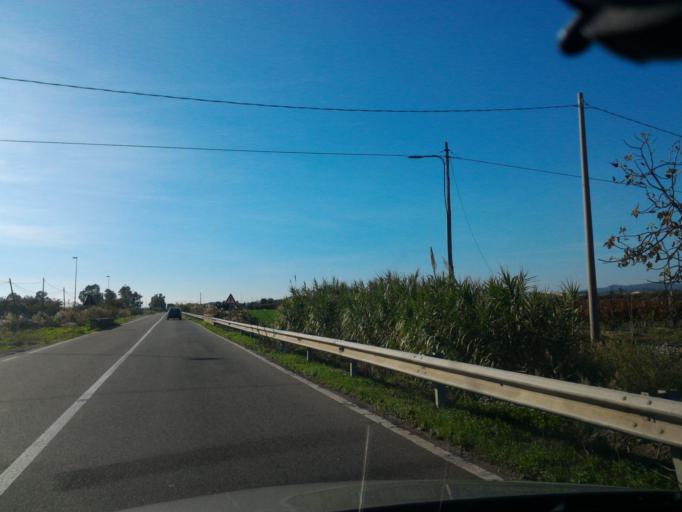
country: IT
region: Calabria
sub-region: Provincia di Crotone
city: Tronca
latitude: 39.1948
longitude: 17.1115
